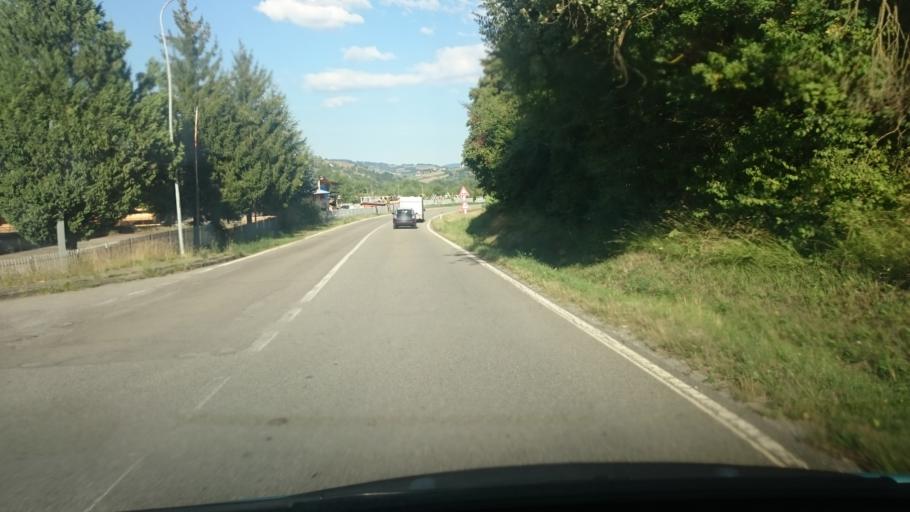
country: IT
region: Emilia-Romagna
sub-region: Provincia di Reggio Emilia
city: Villa Minozzo
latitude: 44.4034
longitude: 10.4813
